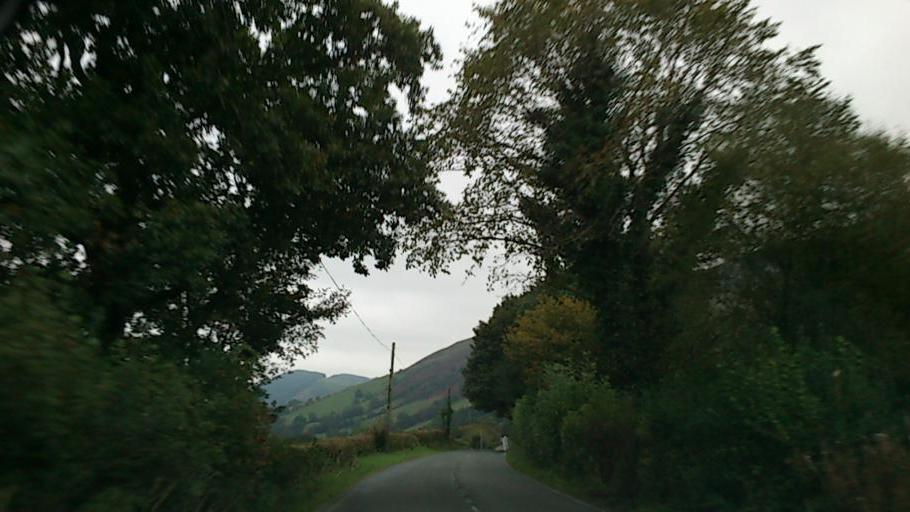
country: GB
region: Wales
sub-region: Gwynedd
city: Corris
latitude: 52.6822
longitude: -3.6970
